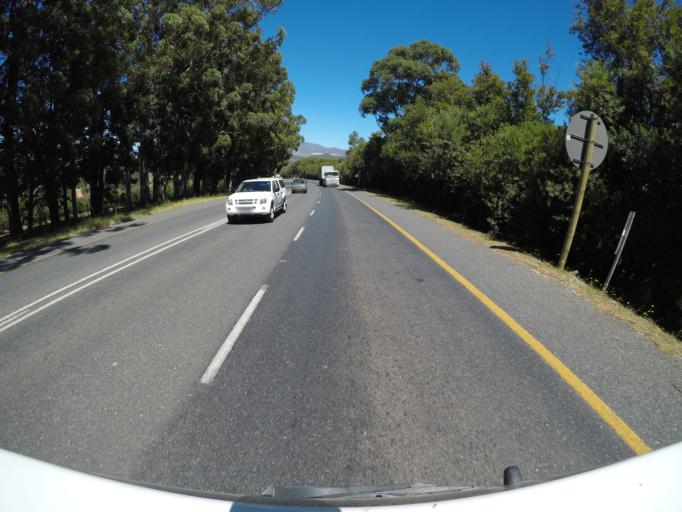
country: ZA
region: Western Cape
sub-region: Overberg District Municipality
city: Grabouw
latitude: -34.1628
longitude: 19.0293
